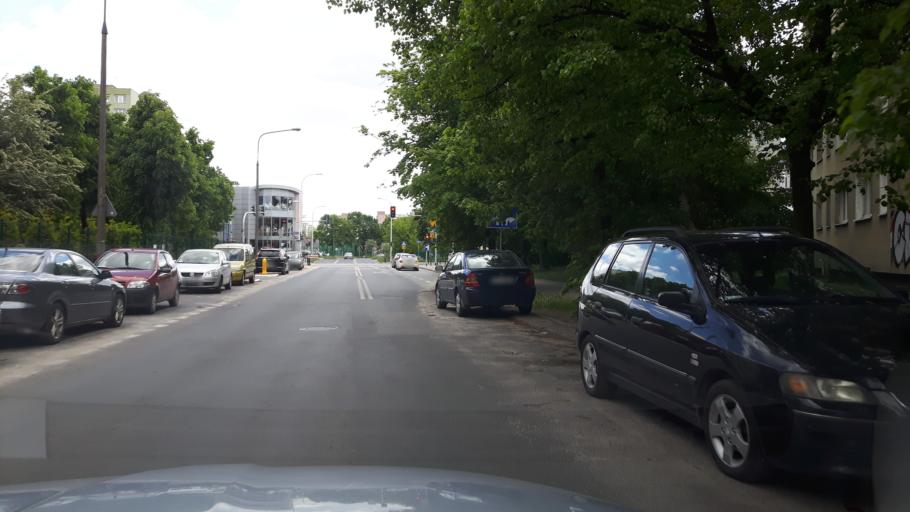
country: PL
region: Masovian Voivodeship
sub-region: Warszawa
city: Targowek
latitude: 52.2935
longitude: 21.0232
